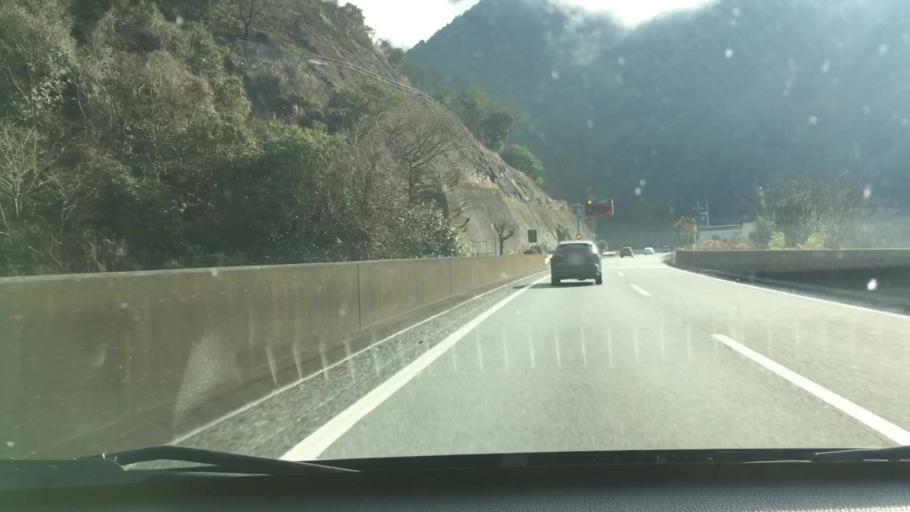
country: JP
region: Kumamoto
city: Yatsushiro
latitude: 32.4274
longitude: 130.7025
